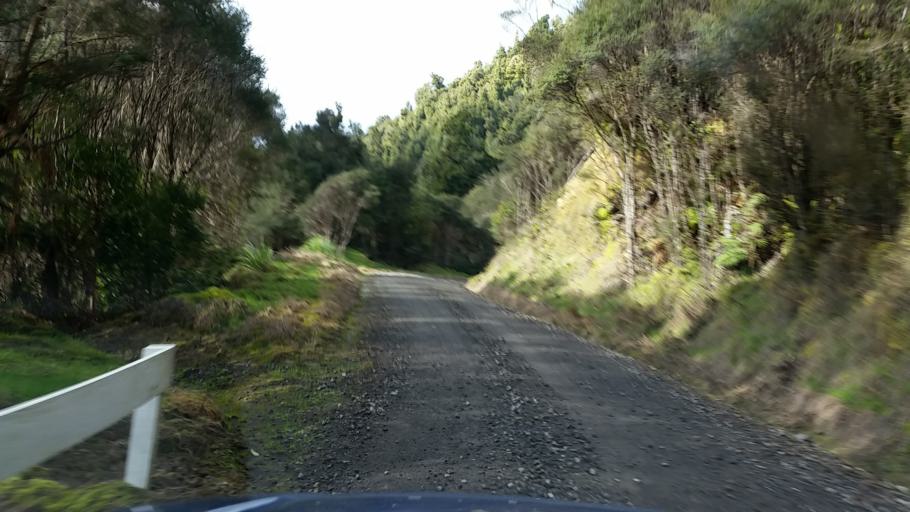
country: NZ
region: Taranaki
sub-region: South Taranaki District
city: Eltham
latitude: -39.2645
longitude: 174.7754
